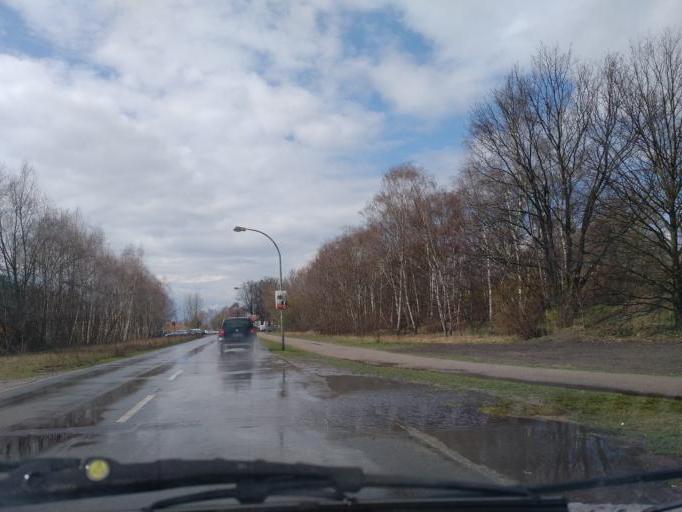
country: DE
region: Brandenburg
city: Falkensee
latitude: 52.5525
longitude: 13.1184
